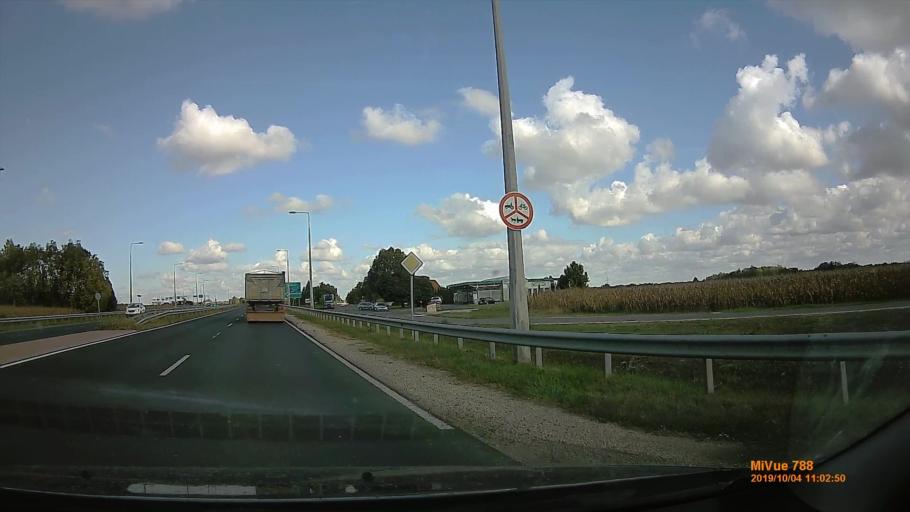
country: HU
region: Somogy
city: Kaposvar
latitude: 46.3914
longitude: 17.7791
